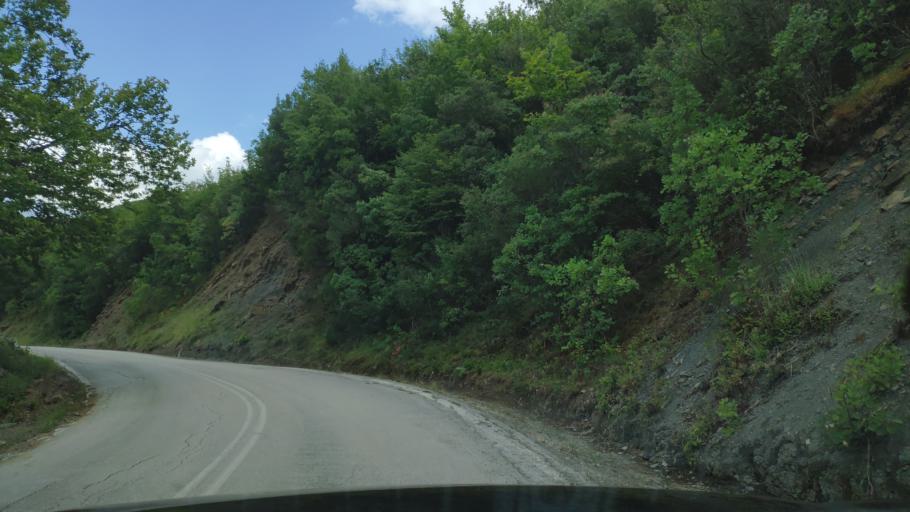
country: GR
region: Epirus
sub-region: Nomos Artas
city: Agios Dimitrios
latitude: 39.4568
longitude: 21.0498
